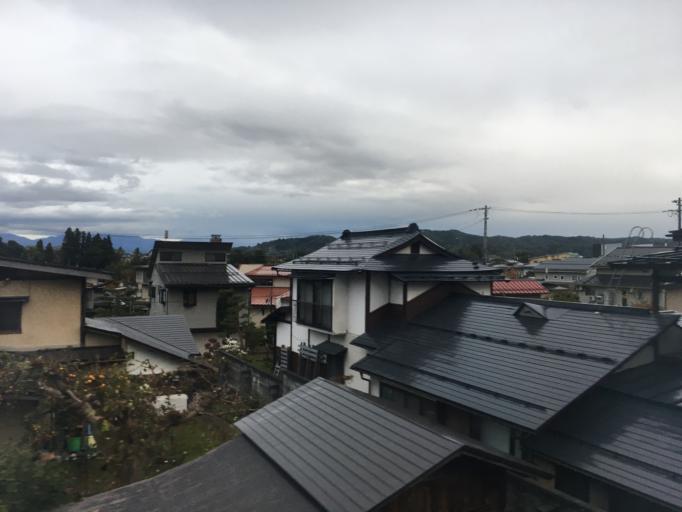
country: JP
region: Yamagata
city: Sagae
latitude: 38.3834
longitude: 140.2105
